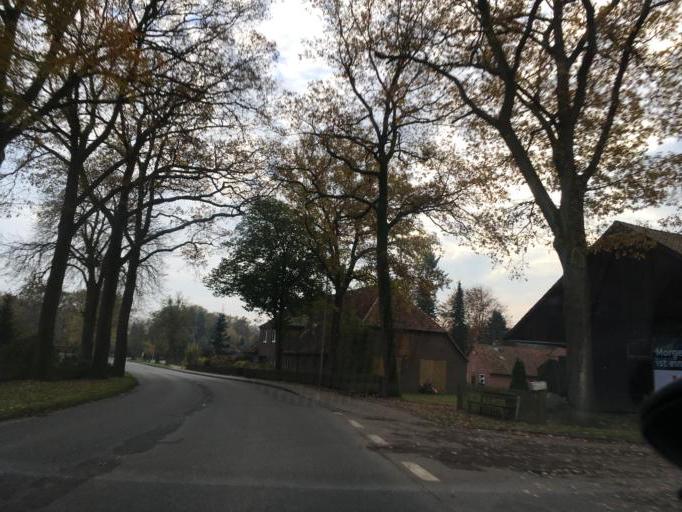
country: DE
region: Lower Saxony
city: Wietzendorf
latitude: 52.9457
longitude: 9.9812
